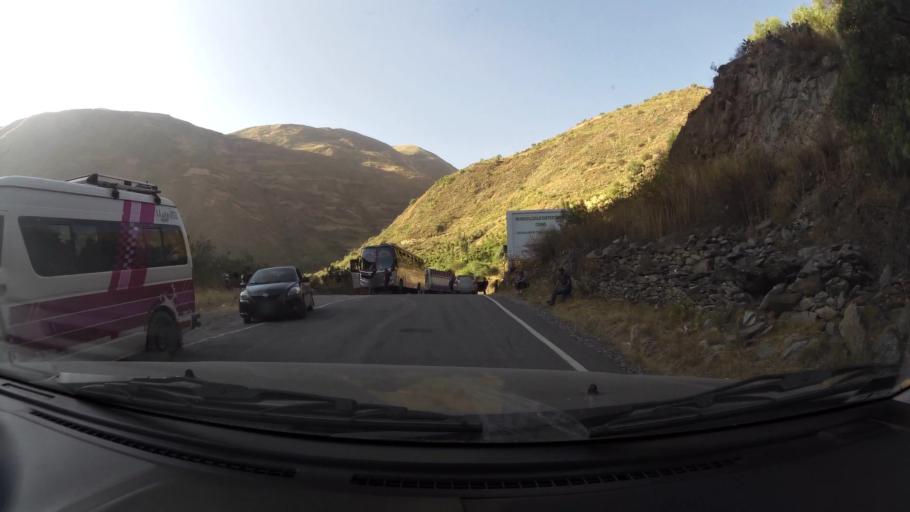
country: PE
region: Huancavelica
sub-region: Provincia de Tayacaja
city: Colcabamba
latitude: -12.5251
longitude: -74.6912
